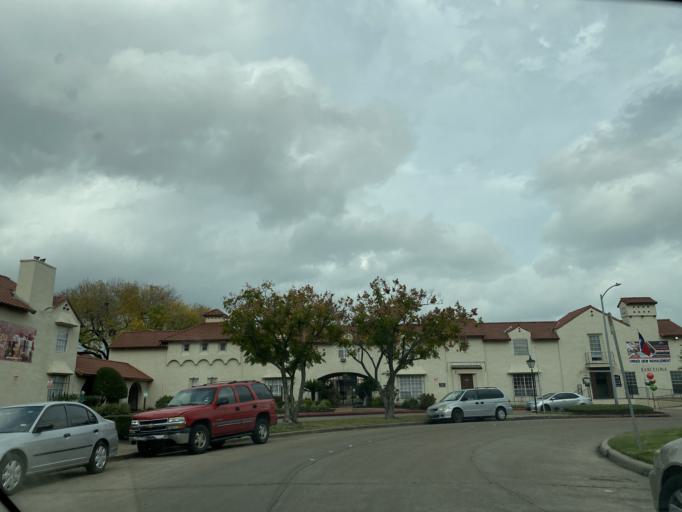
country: US
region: Texas
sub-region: Harris County
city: Piney Point Village
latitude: 29.7407
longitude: -95.4984
